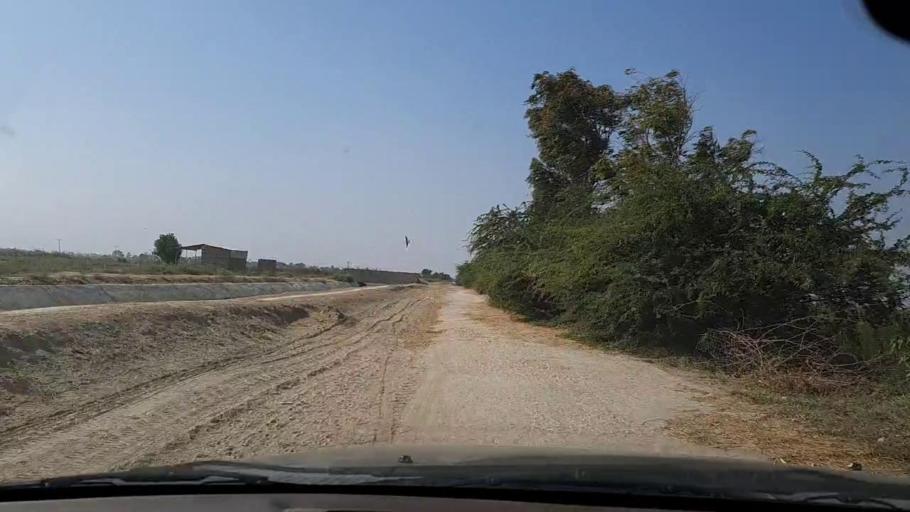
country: PK
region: Sindh
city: Chuhar Jamali
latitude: 24.4276
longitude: 67.8080
